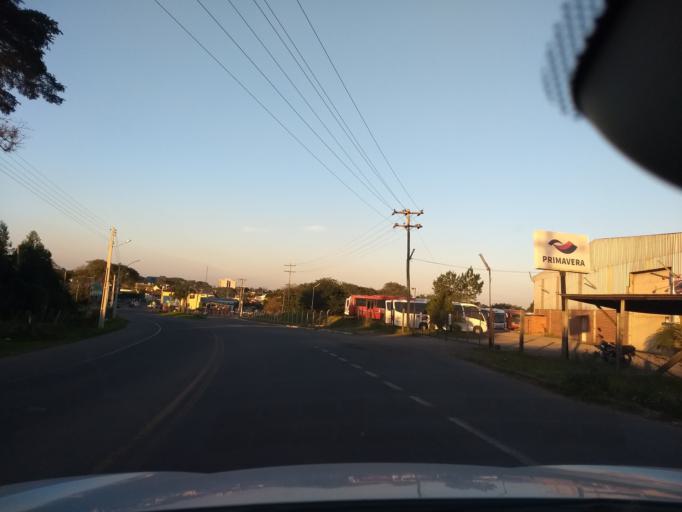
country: BR
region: Rio Grande do Sul
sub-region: Santa Cruz Do Sul
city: Santa Cruz do Sul
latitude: -29.7207
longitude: -52.5181
